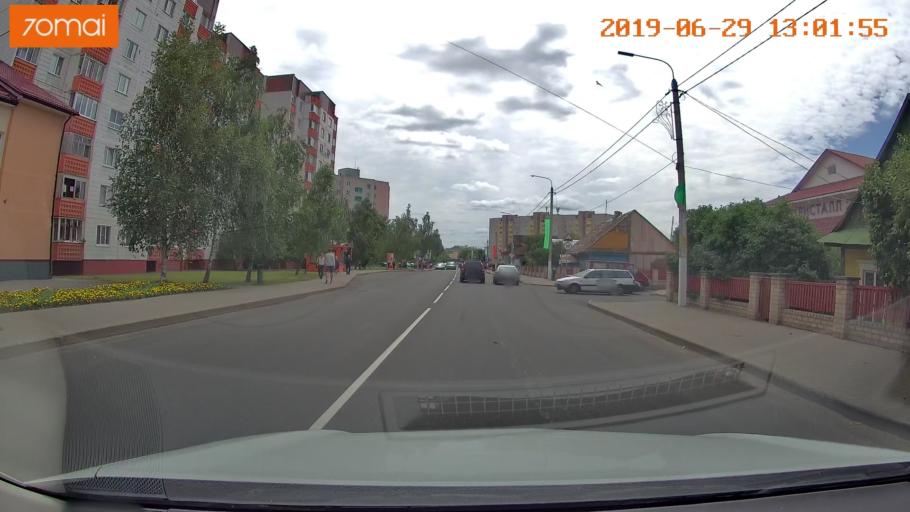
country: BY
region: Minsk
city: Slutsk
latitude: 53.0363
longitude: 27.5598
